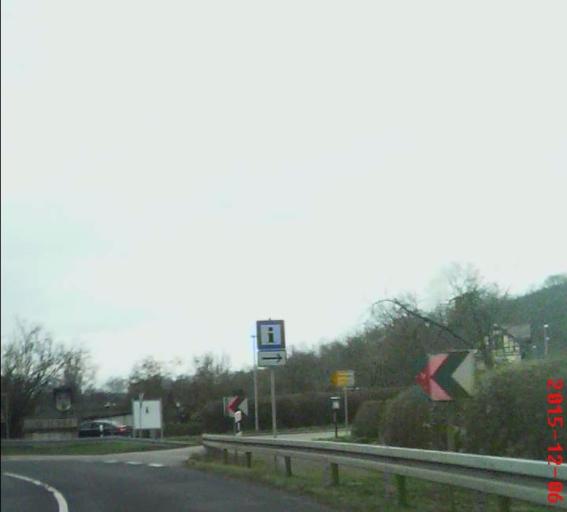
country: DE
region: Thuringia
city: Untermassfeld
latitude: 50.5487
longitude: 10.4119
